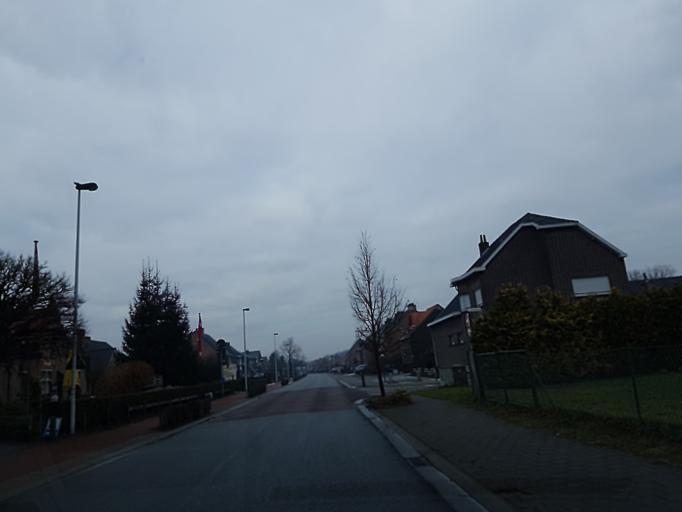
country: BE
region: Flanders
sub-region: Provincie Antwerpen
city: Berlaar
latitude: 51.1427
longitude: 4.6246
